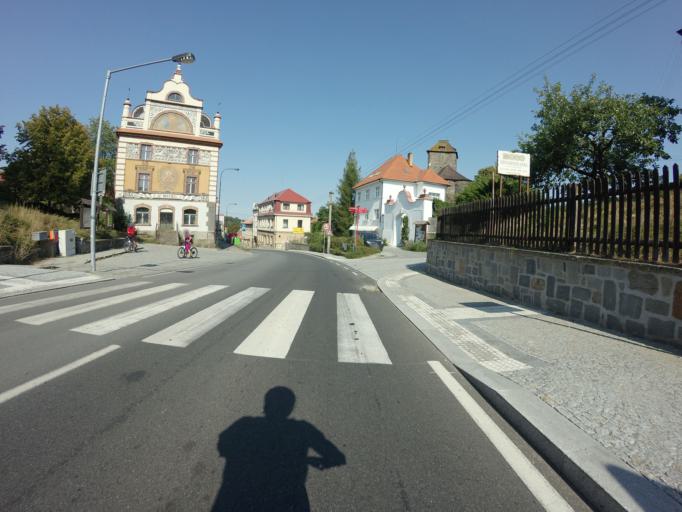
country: CZ
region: Central Bohemia
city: Tynec nad Sazavou
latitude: 49.8298
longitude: 14.5933
